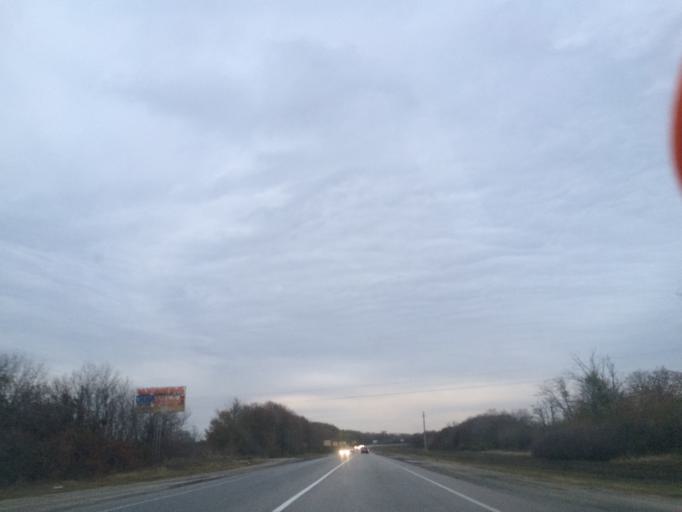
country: RU
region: Rostov
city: Grushevskaya
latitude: 47.4152
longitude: 39.9891
